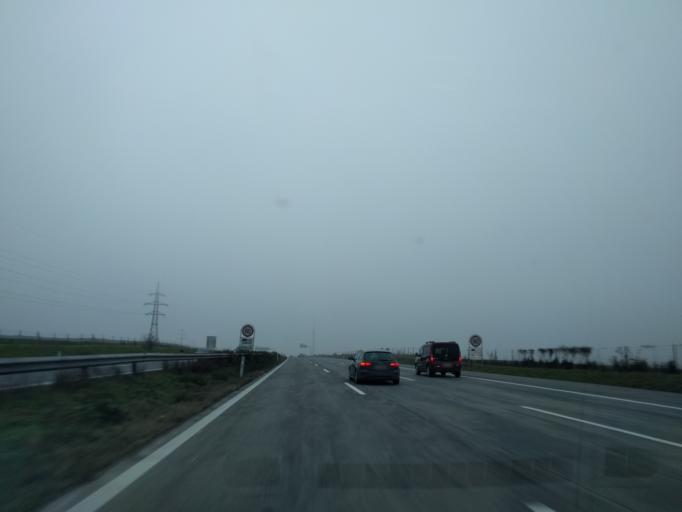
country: AT
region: Lower Austria
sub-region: Sankt Polten Stadt
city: Sankt Poelten
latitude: 48.1779
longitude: 15.5966
